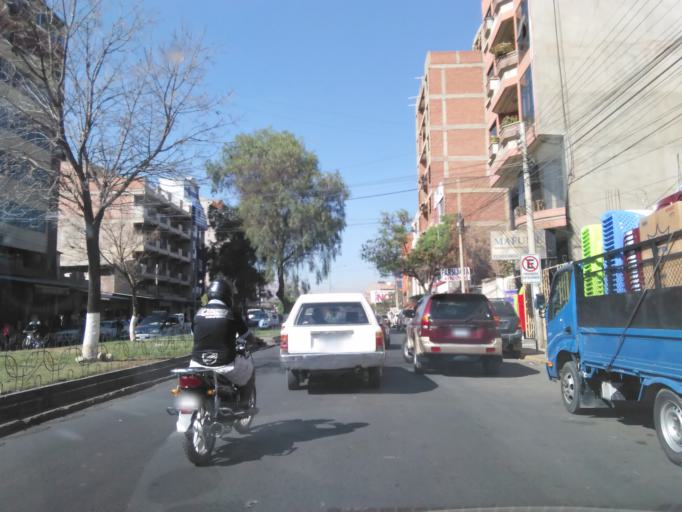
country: BO
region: Cochabamba
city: Cochabamba
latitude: -17.4078
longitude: -66.1566
